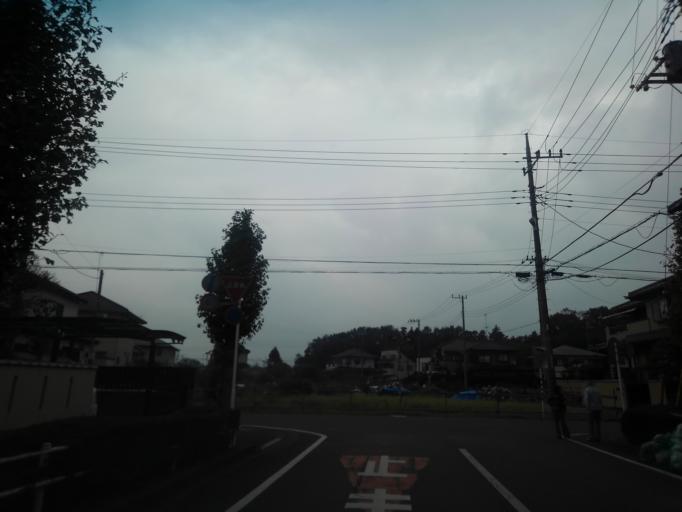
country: JP
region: Saitama
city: Tokorozawa
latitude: 35.8001
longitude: 139.4322
